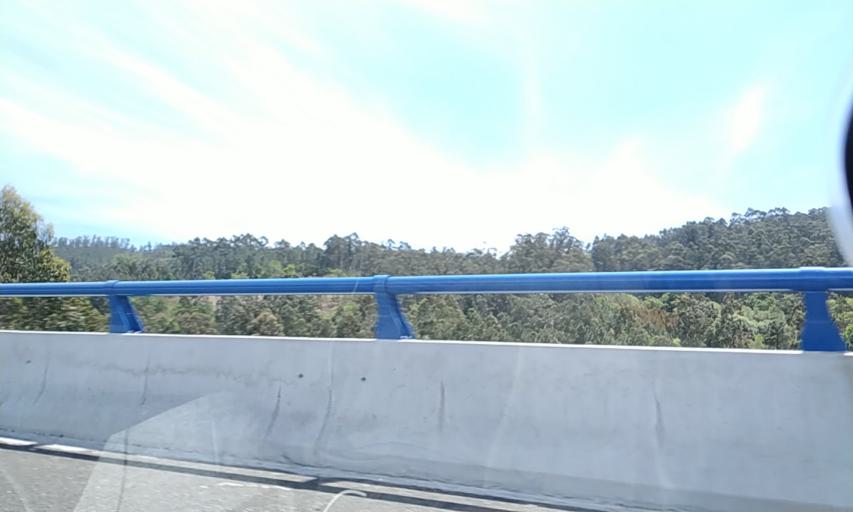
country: ES
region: Galicia
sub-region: Provincia da Coruna
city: Padron
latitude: 42.7975
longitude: -8.6274
